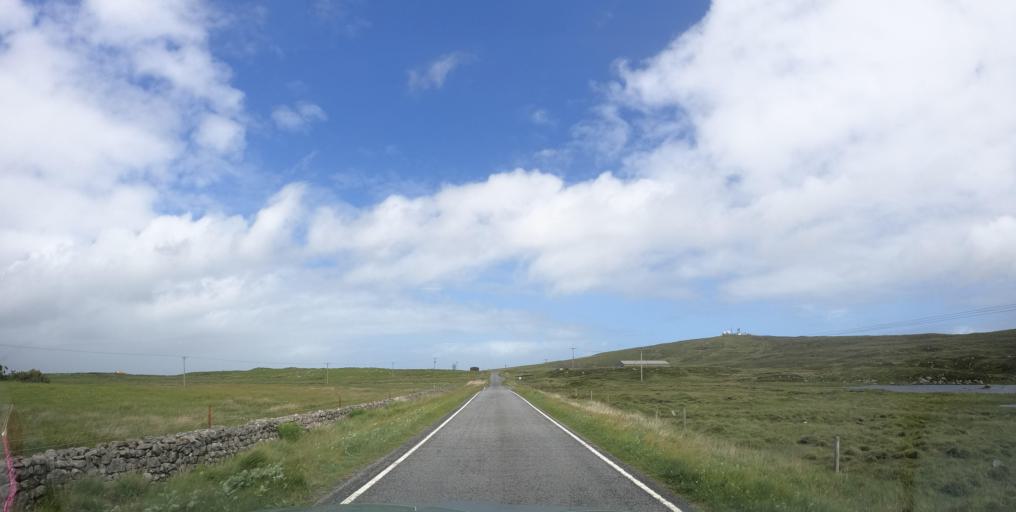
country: GB
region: Scotland
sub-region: Eilean Siar
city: Isle of South Uist
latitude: 57.3331
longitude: -7.3637
